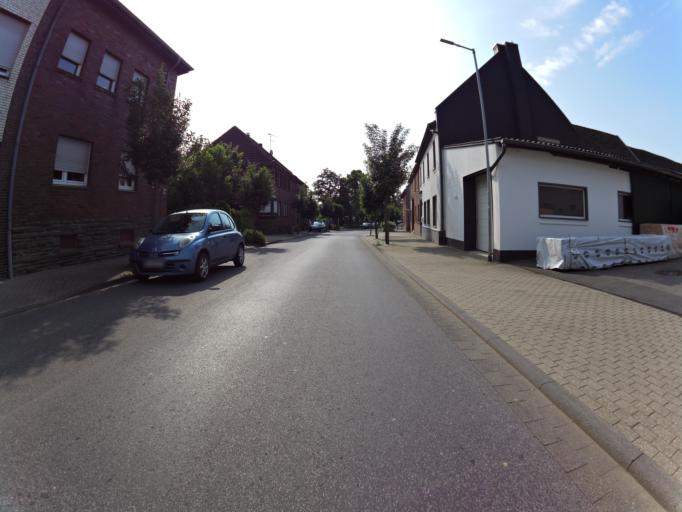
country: DE
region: North Rhine-Westphalia
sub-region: Regierungsbezirk Koln
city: Linnich
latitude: 50.9470
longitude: 6.2492
